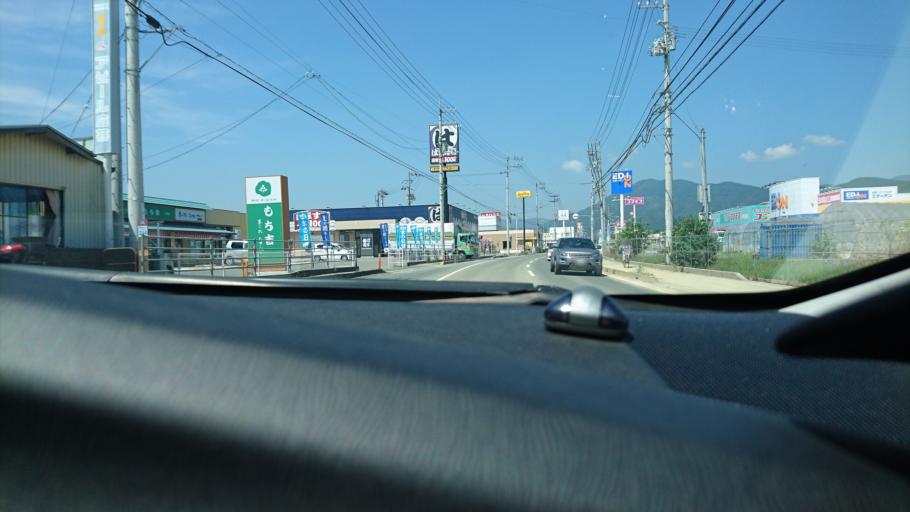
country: JP
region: Ehime
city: Ozu
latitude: 33.5279
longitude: 132.5667
